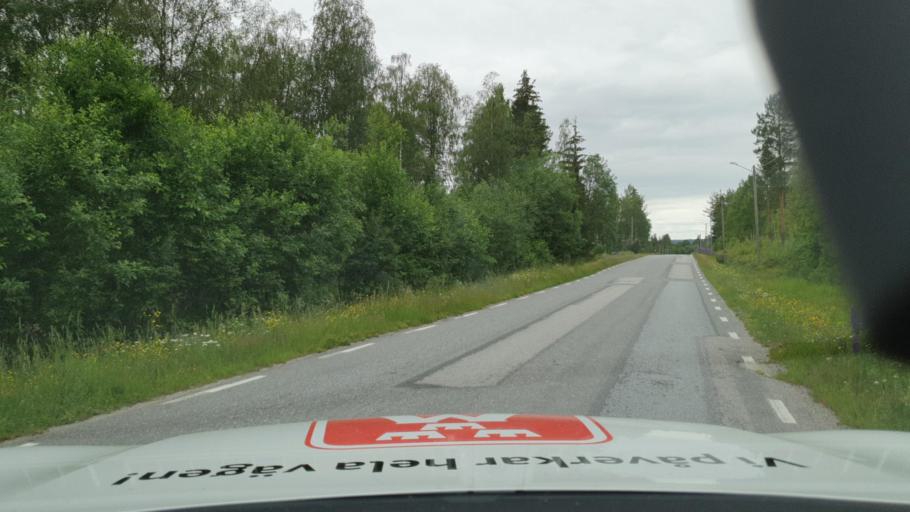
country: SE
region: Vaesterbotten
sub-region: Nordmalings Kommun
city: Nordmaling
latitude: 63.5280
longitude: 19.4106
